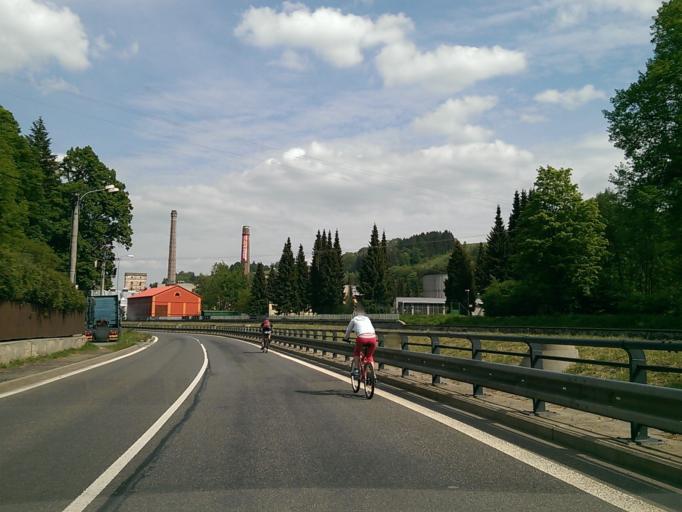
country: CZ
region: Liberecky
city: Zelezny Brod
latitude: 50.6409
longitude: 15.2411
